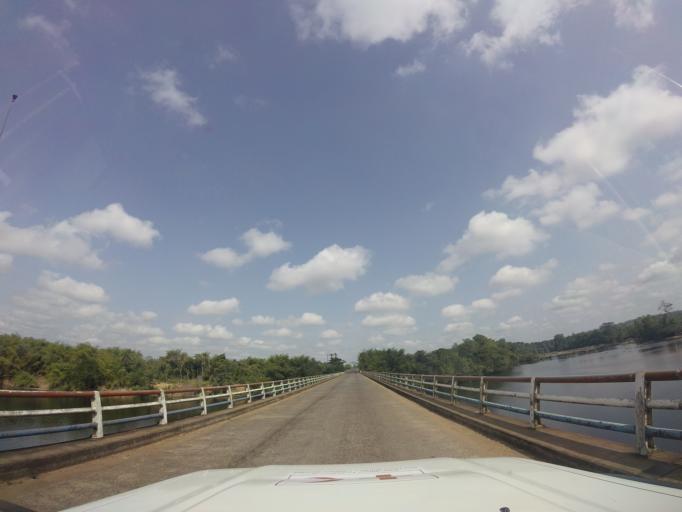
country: LR
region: Bomi
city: Tubmanburg
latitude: 6.7197
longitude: -10.9781
